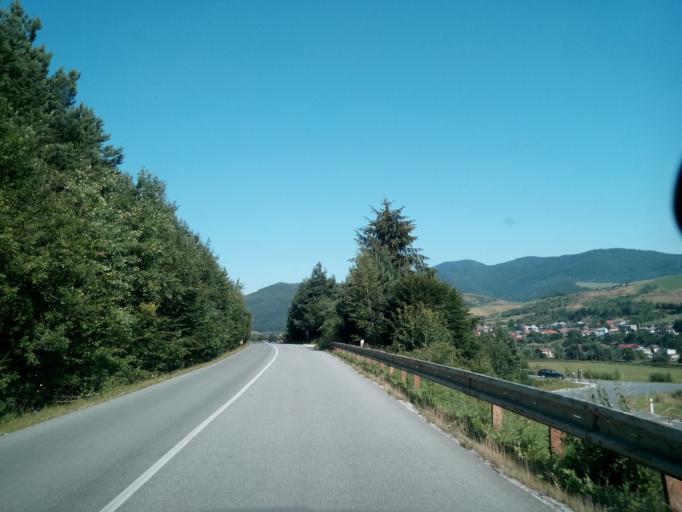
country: SK
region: Kosicky
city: Krompachy
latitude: 48.9187
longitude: 20.9305
